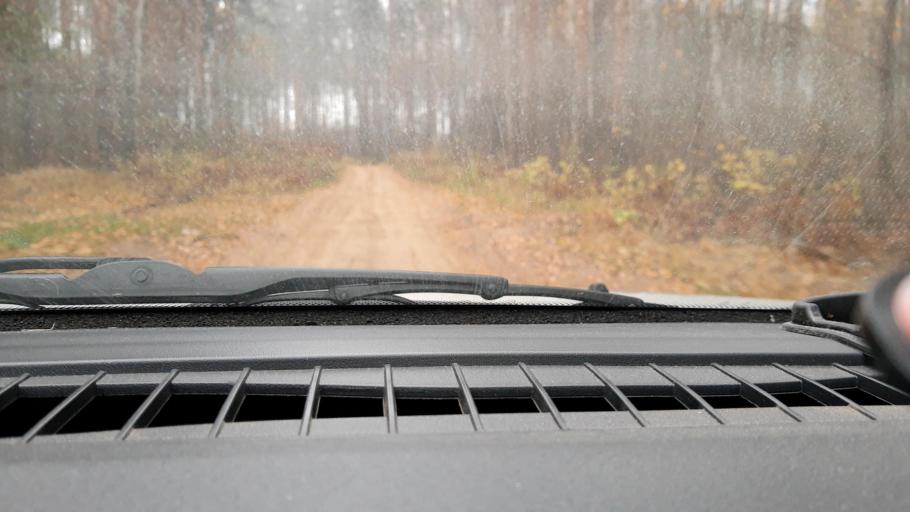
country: RU
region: Nizjnij Novgorod
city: Sitniki
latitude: 56.4328
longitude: 44.0651
